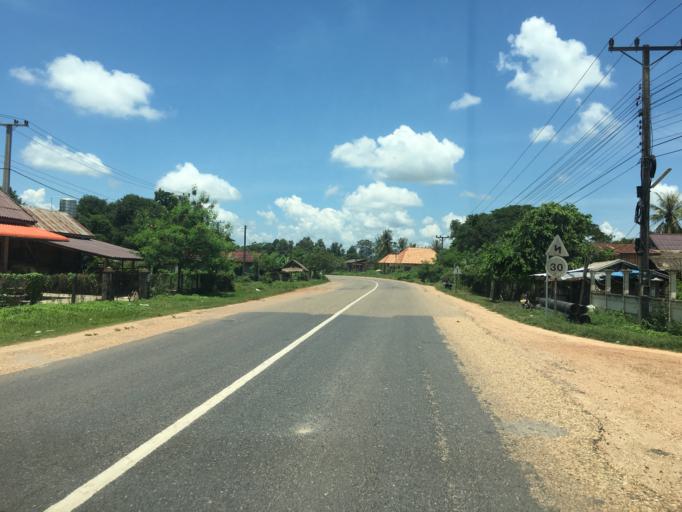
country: LA
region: Vientiane
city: Muang Phon-Hong
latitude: 18.2363
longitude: 102.4883
